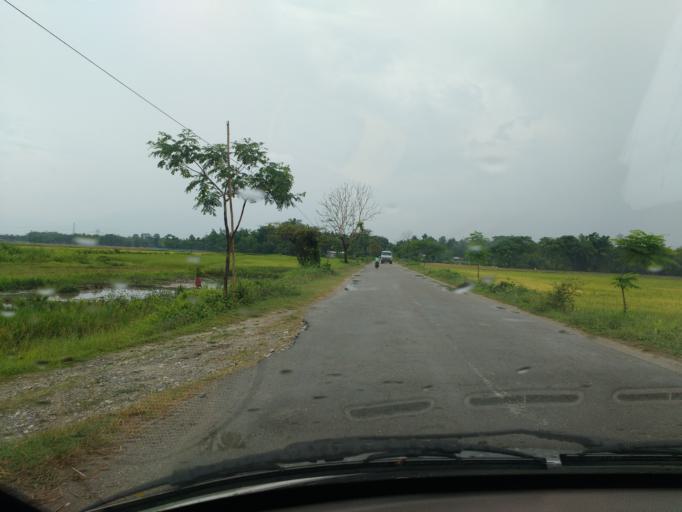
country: IN
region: Assam
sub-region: Udalguri
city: Udalguri
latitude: 26.7250
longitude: 92.2109
